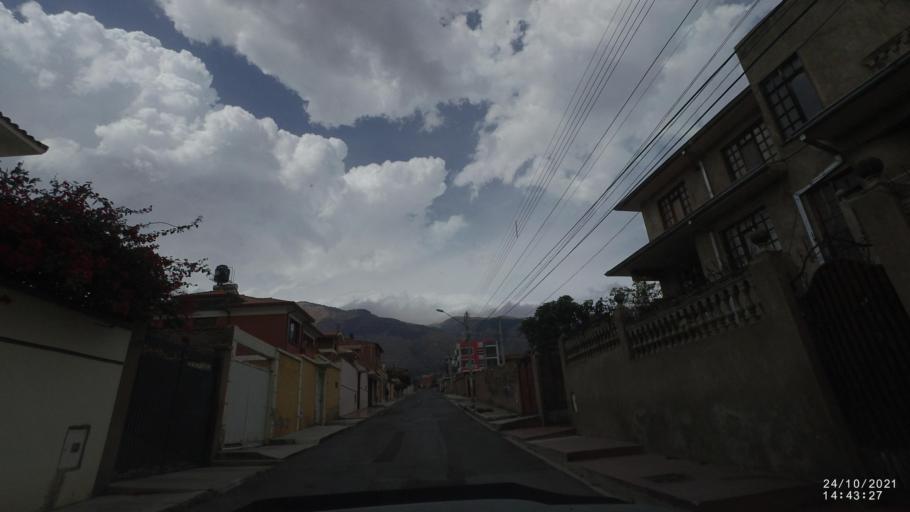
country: BO
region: Cochabamba
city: Cochabamba
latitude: -17.3477
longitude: -66.1755
